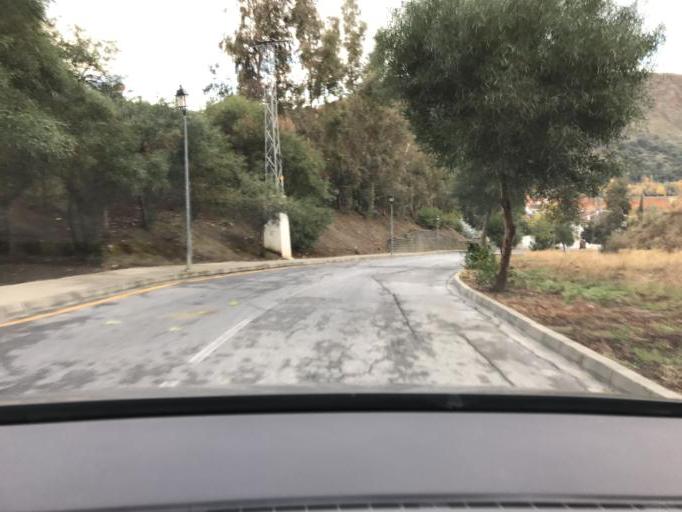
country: ES
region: Andalusia
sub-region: Provincia de Granada
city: Cenes de la Vega
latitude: 37.1641
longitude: -3.5469
